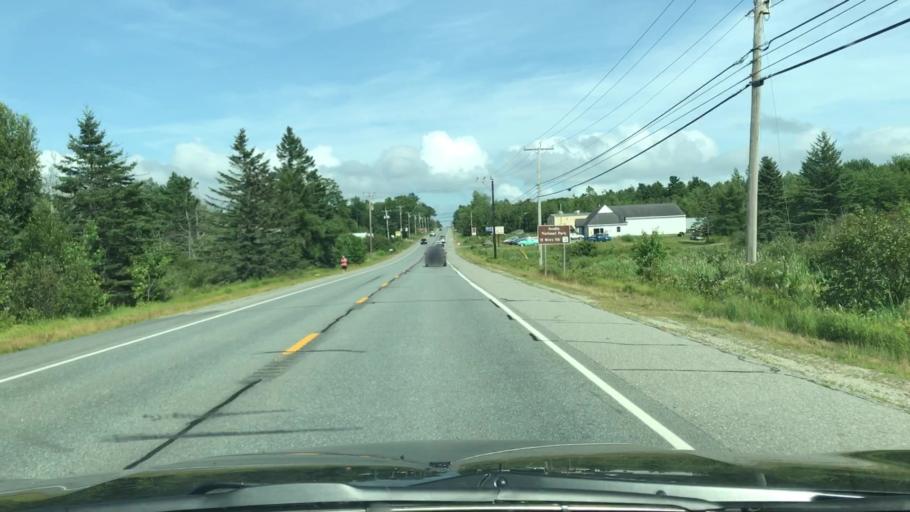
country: US
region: Maine
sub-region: Hancock County
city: Ellsworth
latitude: 44.5395
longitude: -68.4574
